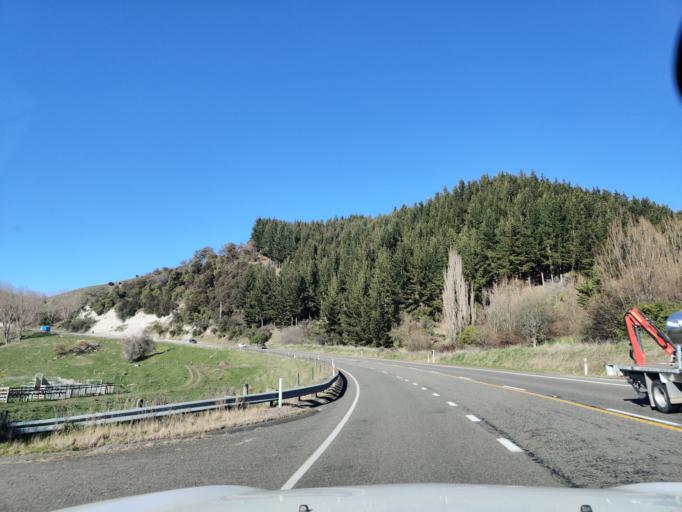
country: NZ
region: Manawatu-Wanganui
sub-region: Ruapehu District
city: Waiouru
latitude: -39.8222
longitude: 175.7765
